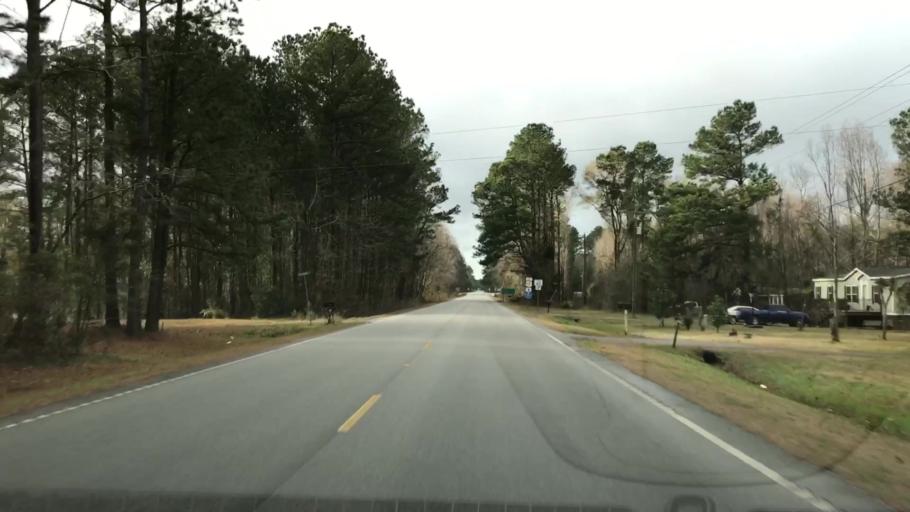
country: US
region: South Carolina
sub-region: Berkeley County
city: Saint Stephen
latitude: 33.2858
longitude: -79.7533
